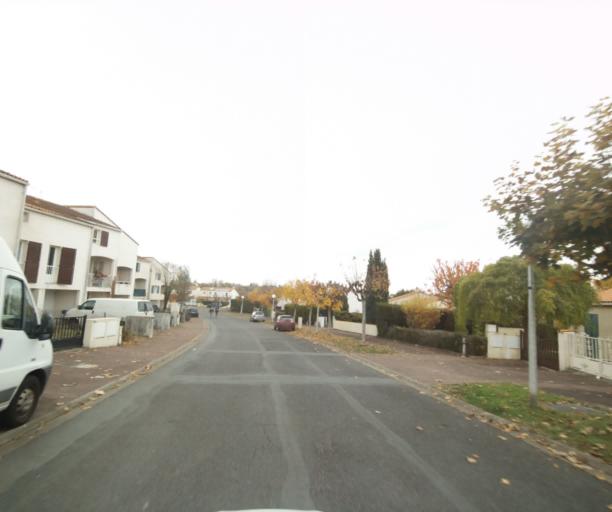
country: FR
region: Poitou-Charentes
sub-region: Departement de la Charente-Maritime
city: Saintes
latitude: 45.7385
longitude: -0.6494
